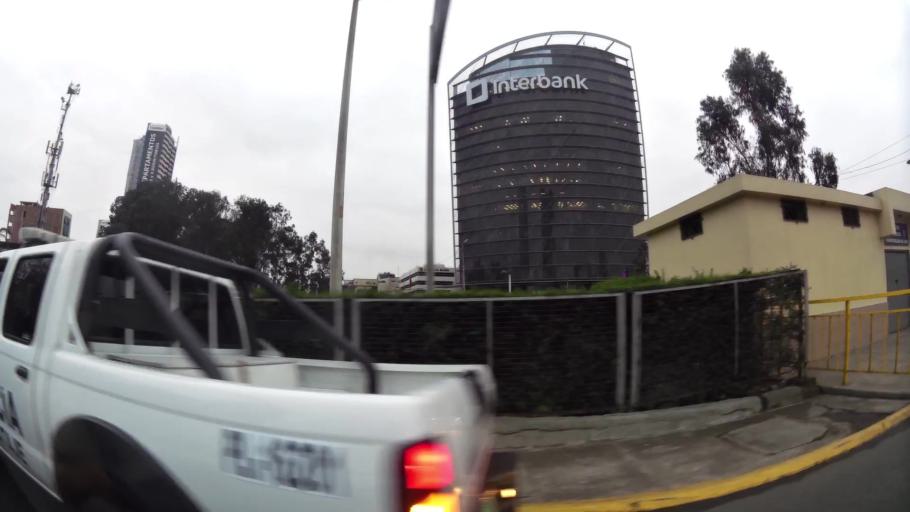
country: PE
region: Lima
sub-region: Lima
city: San Luis
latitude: -12.0907
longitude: -77.0233
